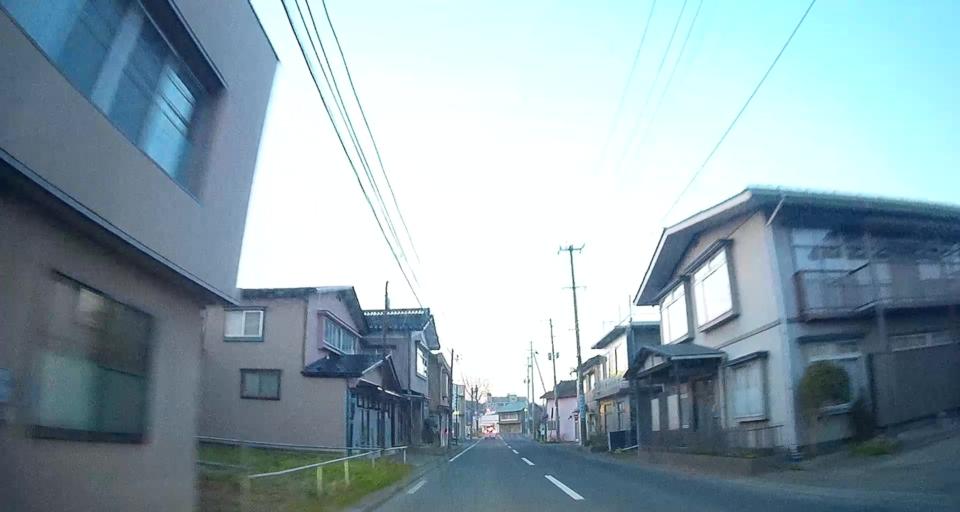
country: JP
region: Aomori
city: Hachinohe
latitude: 40.1855
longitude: 141.7718
